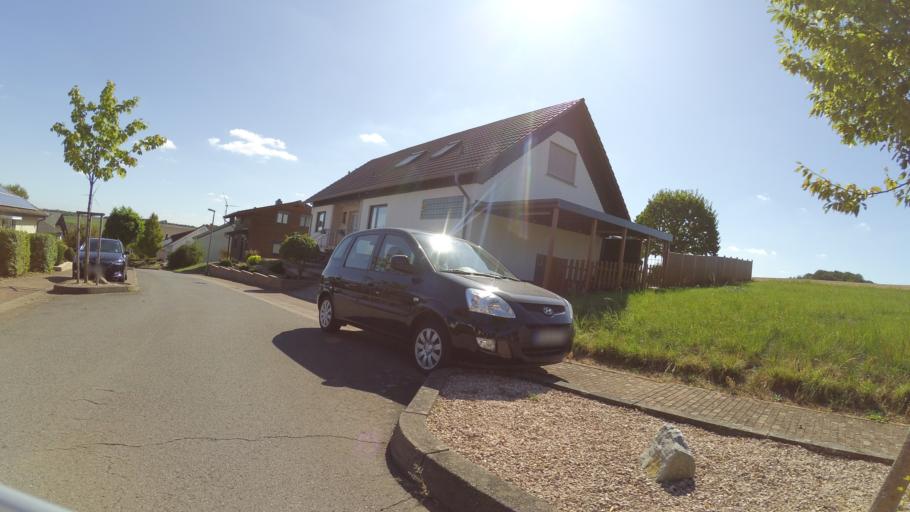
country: DE
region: Saarland
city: Lebach
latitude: 49.3901
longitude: 6.9000
